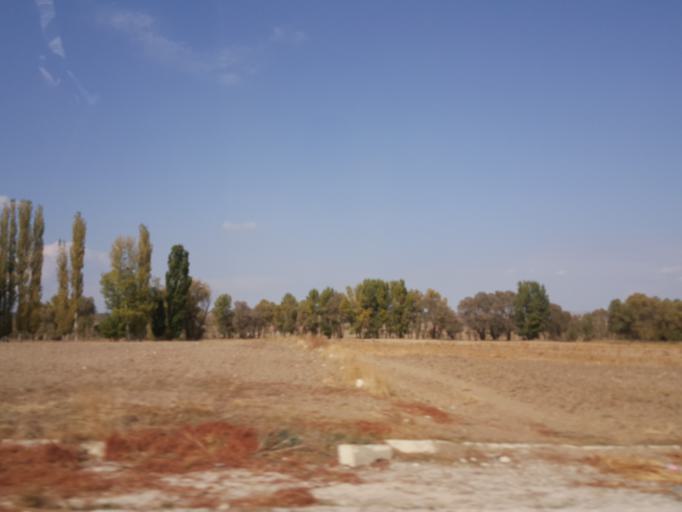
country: TR
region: Corum
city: Alaca
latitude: 40.1444
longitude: 34.8319
